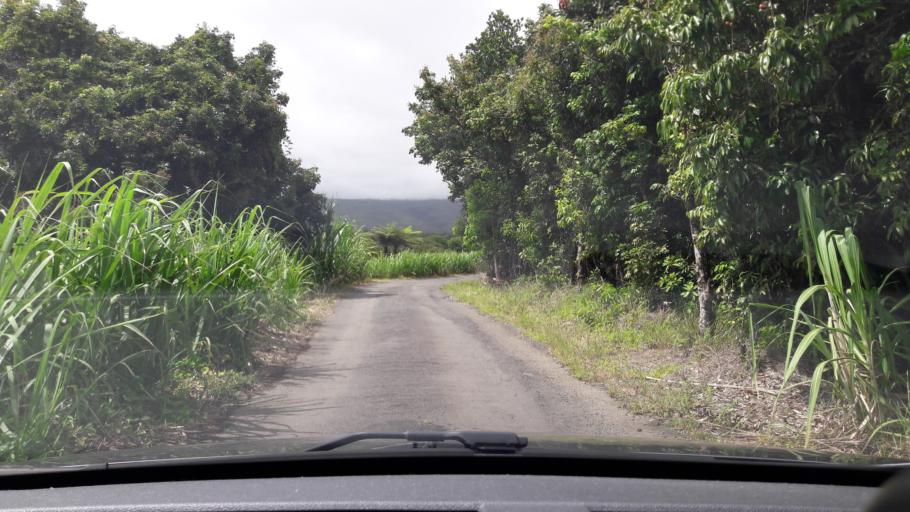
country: RE
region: Reunion
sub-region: Reunion
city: Saint-Benoit
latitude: -21.0972
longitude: 55.6987
